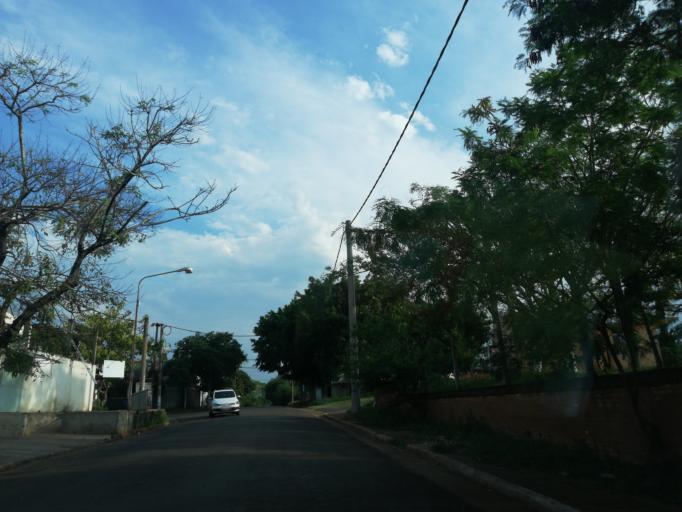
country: AR
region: Misiones
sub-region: Departamento de Capital
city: Posadas
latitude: -27.3678
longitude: -55.9531
